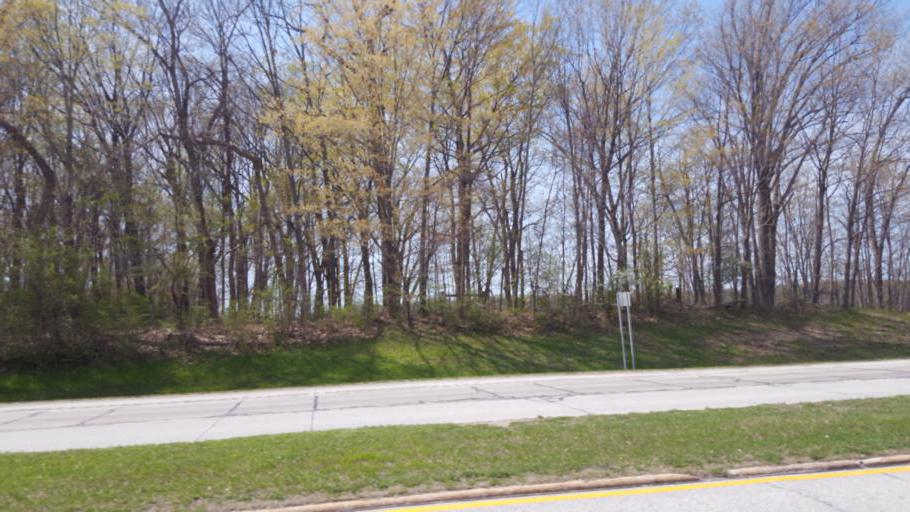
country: US
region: Ohio
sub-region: Lake County
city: Fairport Harbor
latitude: 41.7327
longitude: -81.2902
